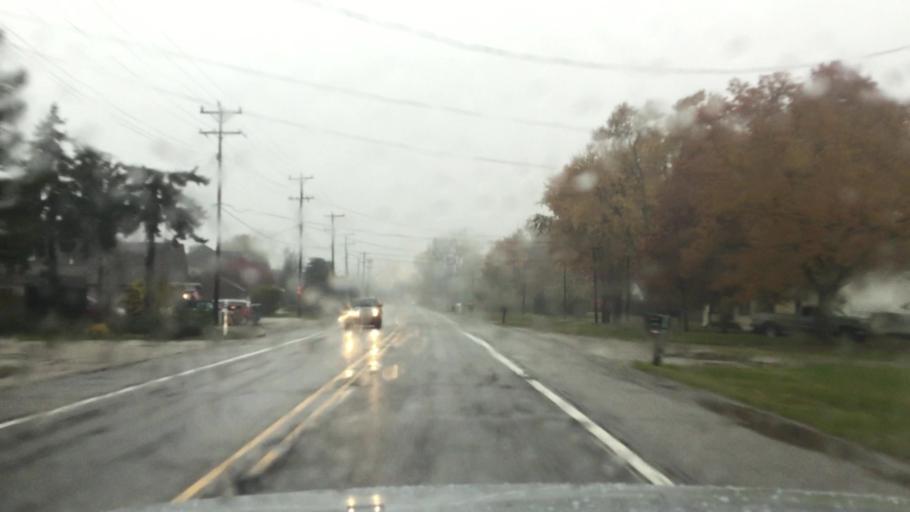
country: US
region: Michigan
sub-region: Macomb County
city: New Baltimore
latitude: 42.6899
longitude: -82.6802
